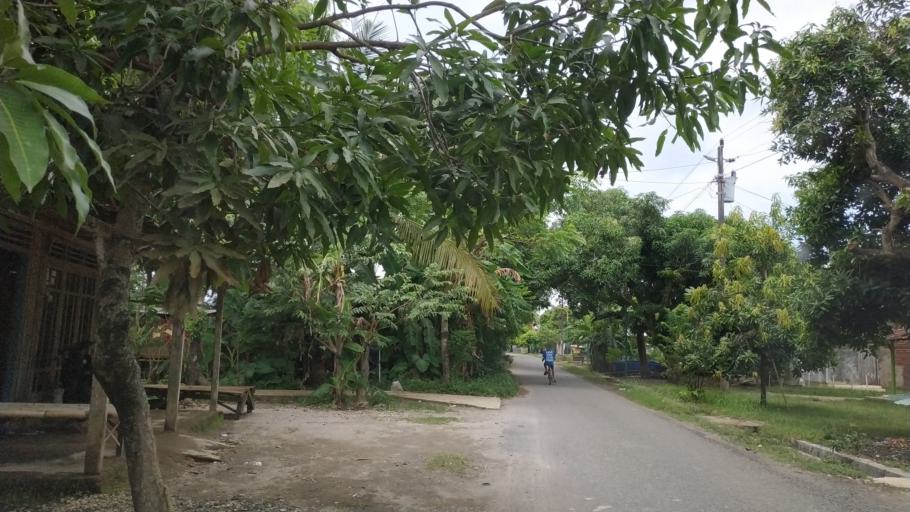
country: ID
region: Central Java
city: Krajan Tegalombo
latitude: -6.4219
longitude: 110.9803
